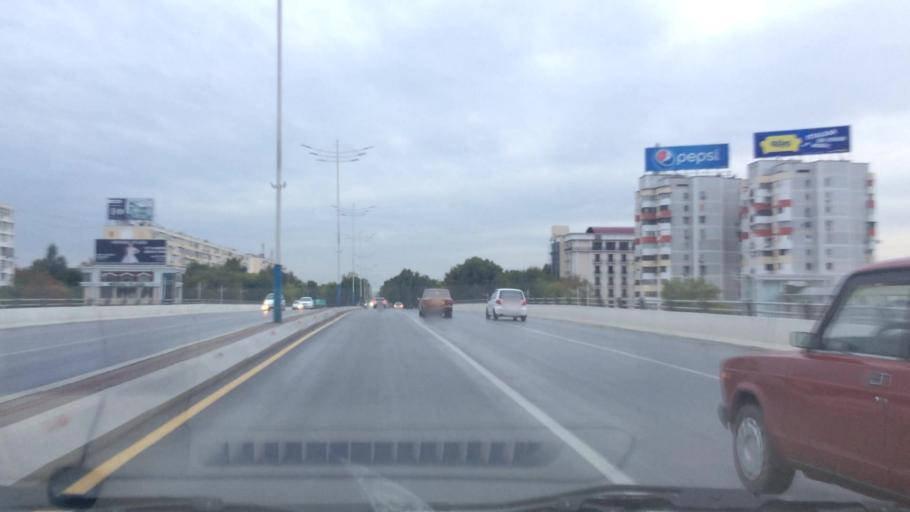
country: UZ
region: Toshkent Shahri
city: Tashkent
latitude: 41.2925
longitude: 69.2238
